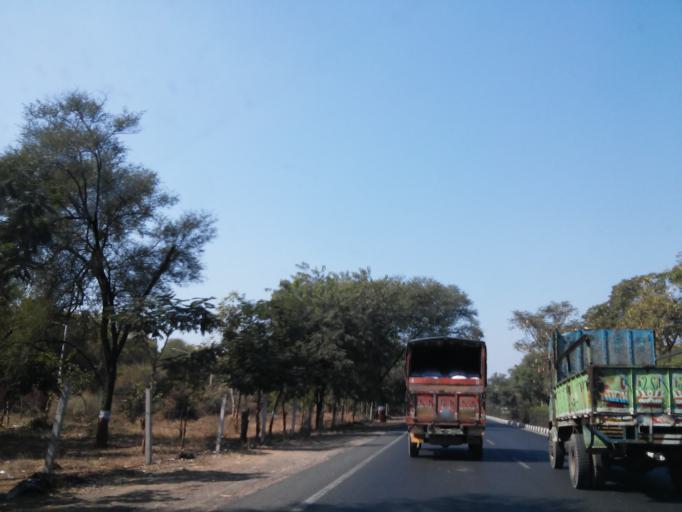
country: IN
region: Gujarat
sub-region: Gandhinagar
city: Ghandinagar
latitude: 23.2364
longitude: 72.7143
